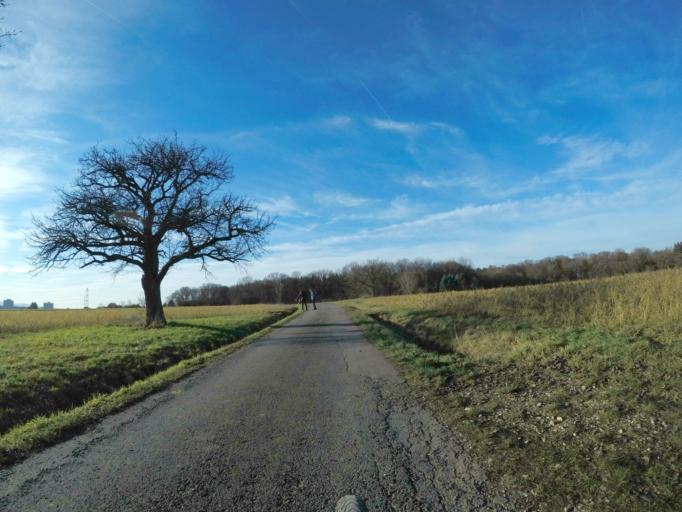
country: DE
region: Baden-Wuerttemberg
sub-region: Tuebingen Region
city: Eningen unter Achalm
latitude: 48.5208
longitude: 9.2465
